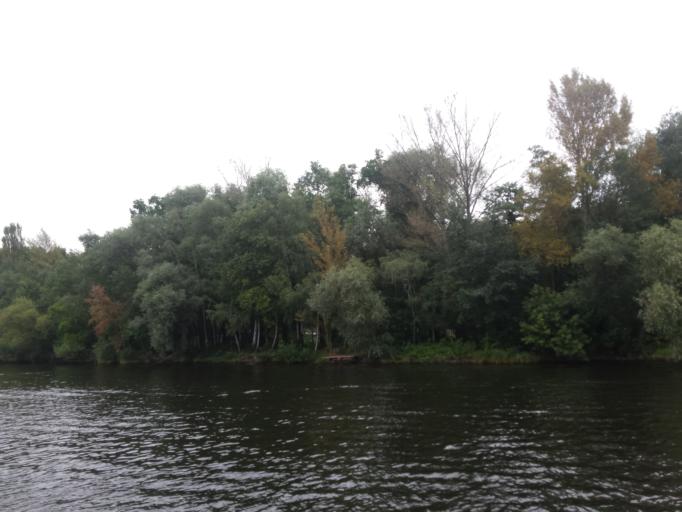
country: DE
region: Brandenburg
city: Potsdam
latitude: 52.4250
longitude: 13.1016
